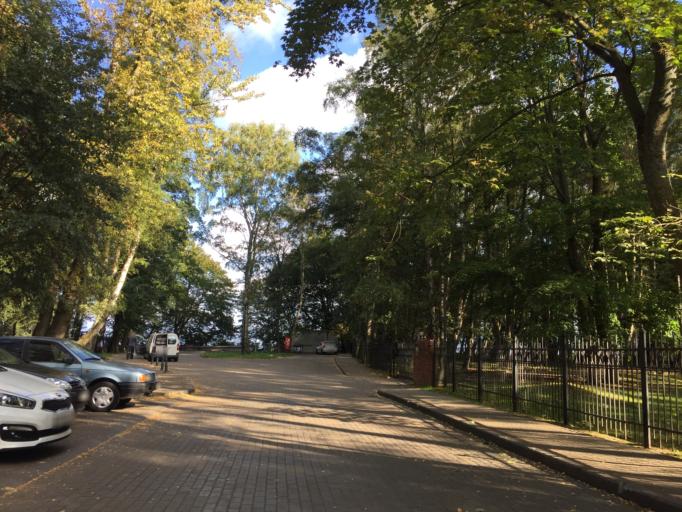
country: RU
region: Kaliningrad
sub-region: Gorod Svetlogorsk
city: Svetlogorsk
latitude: 54.9468
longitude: 20.1651
